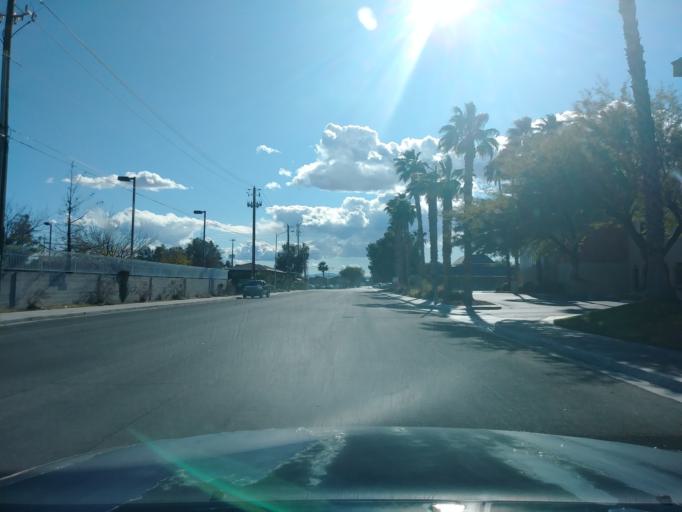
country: US
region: Nevada
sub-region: Clark County
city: Spring Valley
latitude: 36.1460
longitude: -115.2146
